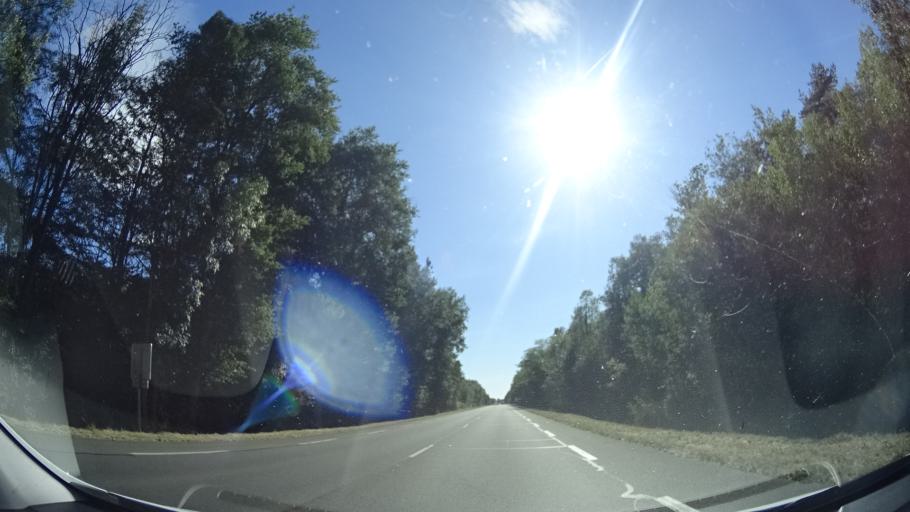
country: FR
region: Centre
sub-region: Departement du Loiret
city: Vitry-aux-Loges
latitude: 47.9014
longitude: 2.2864
